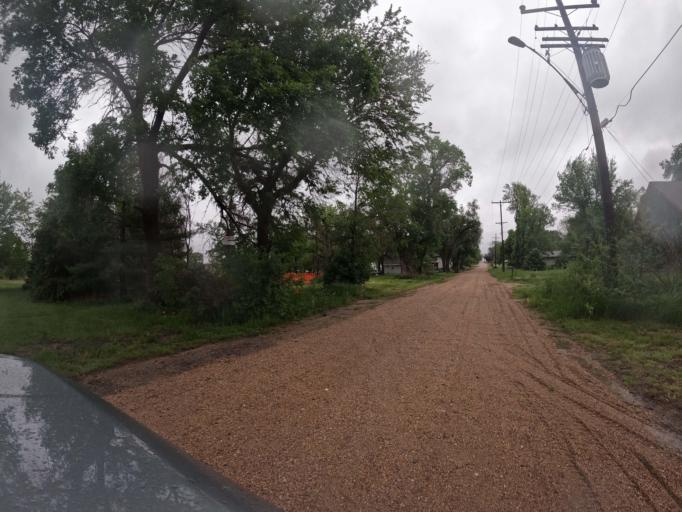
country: US
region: Nebraska
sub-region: Clay County
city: Harvard
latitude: 40.6153
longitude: -98.0999
